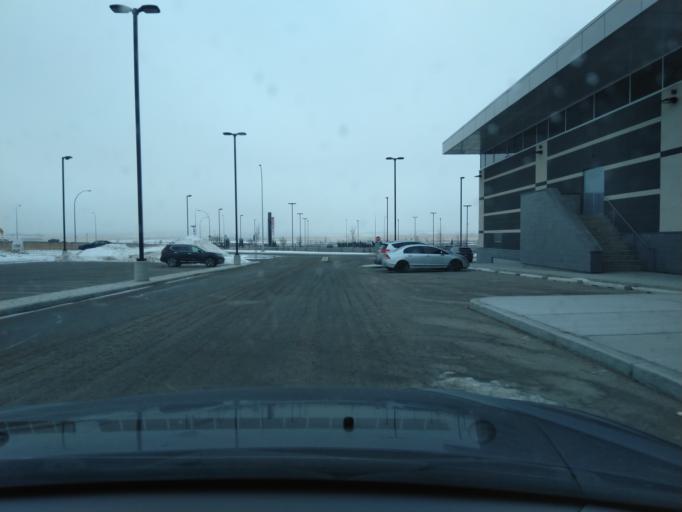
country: CA
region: Alberta
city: Airdrie
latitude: 51.1956
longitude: -113.9973
